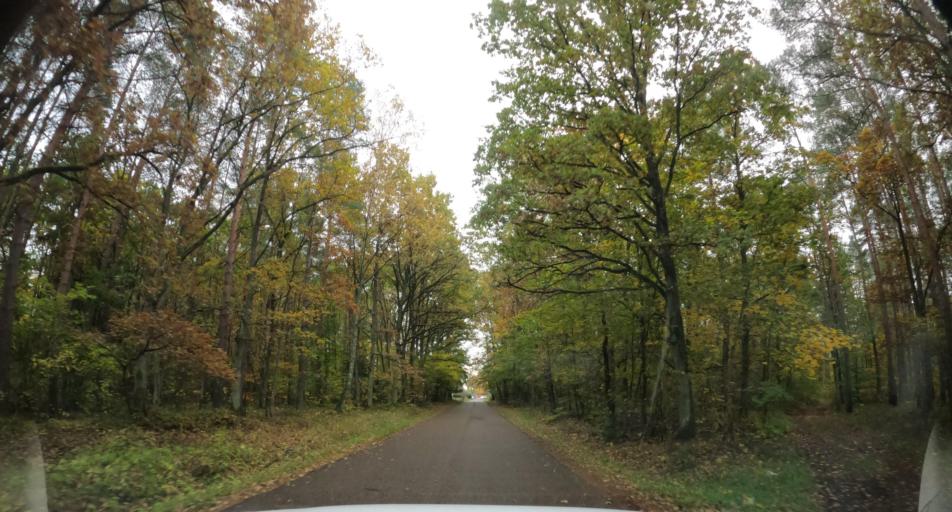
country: PL
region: West Pomeranian Voivodeship
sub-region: Powiat kamienski
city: Wolin
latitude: 53.9105
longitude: 14.5680
